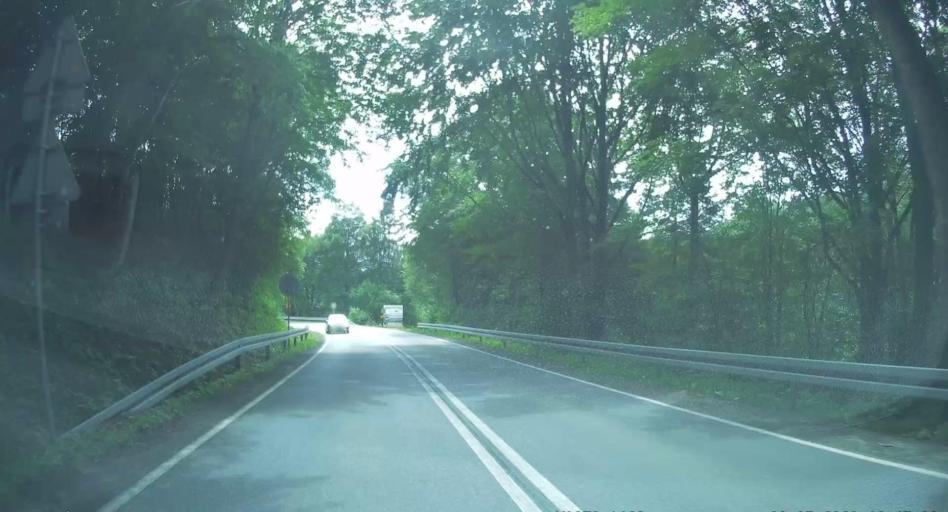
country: PL
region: Lesser Poland Voivodeship
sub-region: Powiat nowosadecki
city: Muszyna
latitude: 49.3483
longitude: 20.8019
